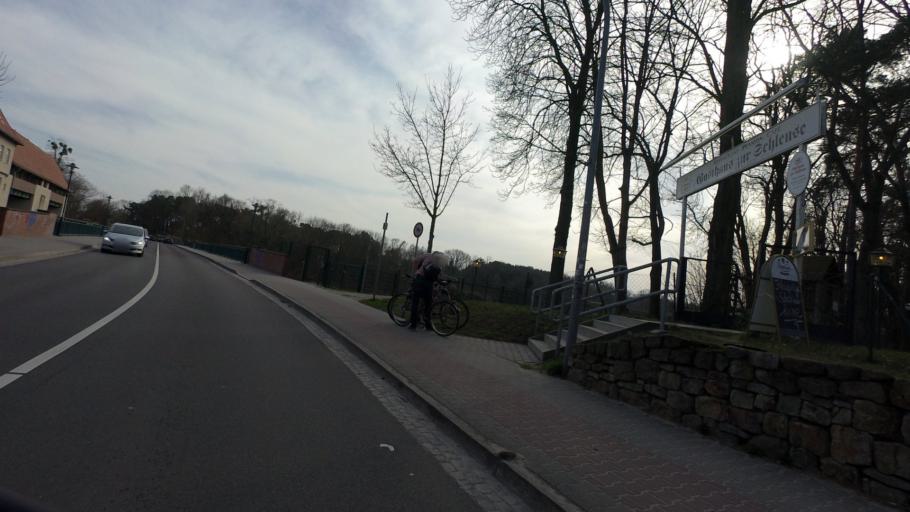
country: DE
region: Brandenburg
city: Stahnsdorf
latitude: 52.3966
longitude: 13.2078
